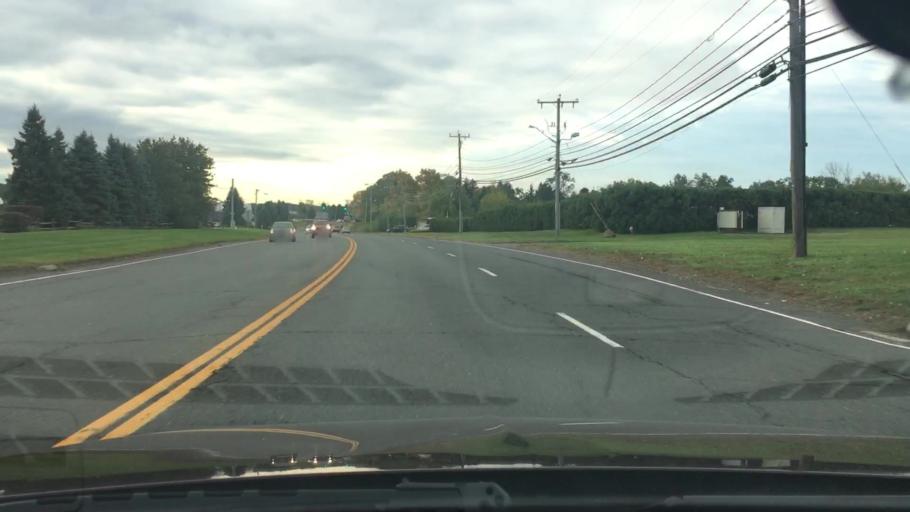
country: US
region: Connecticut
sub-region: Hartford County
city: Windsor Locks
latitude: 41.8896
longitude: -72.6082
